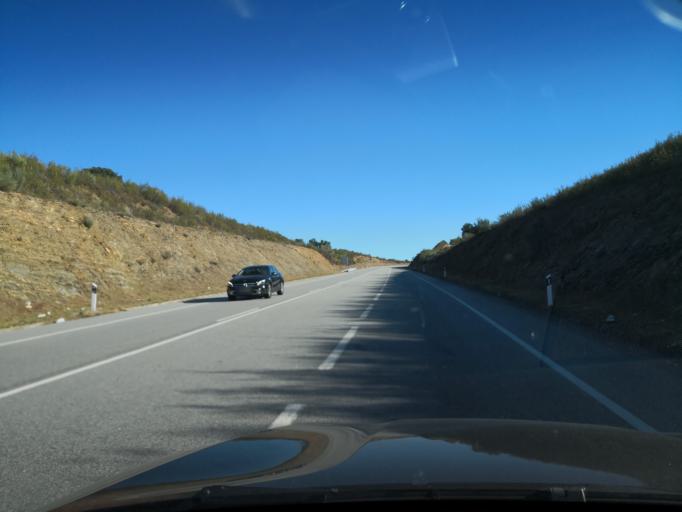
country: PT
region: Braganca
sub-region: Mirandela
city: Mirandela
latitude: 41.4912
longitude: -7.2259
